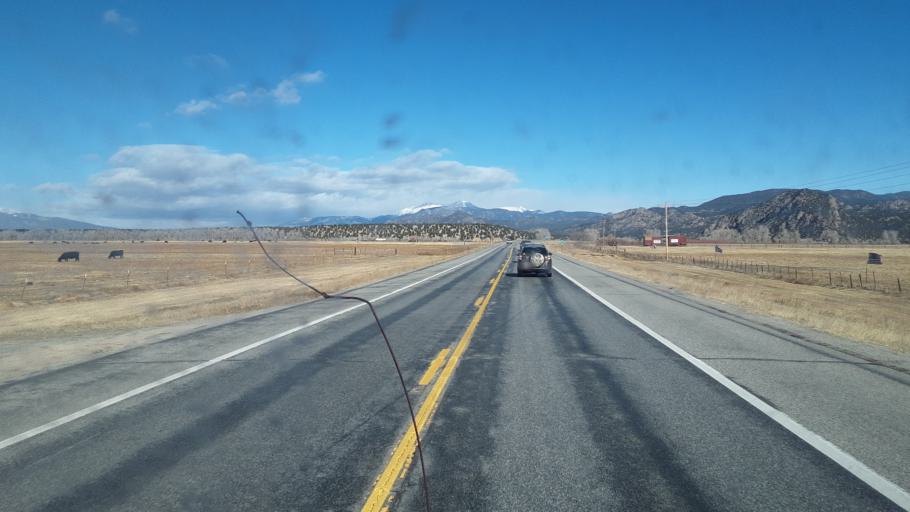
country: US
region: Colorado
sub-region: Chaffee County
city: Buena Vista
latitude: 38.7318
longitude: -106.0859
